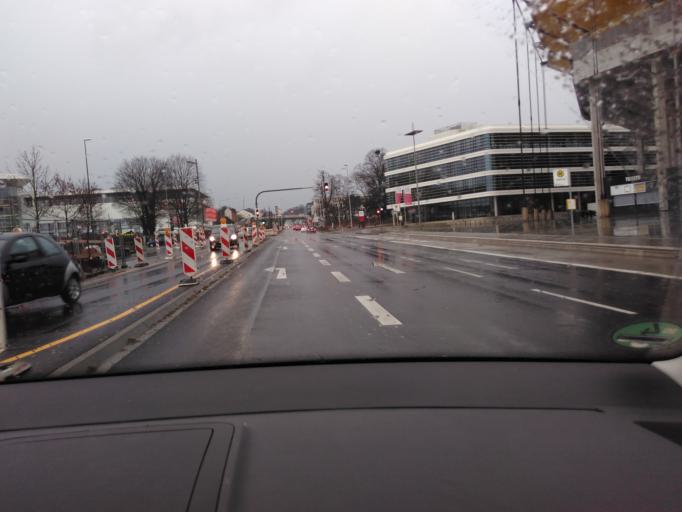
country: DE
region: North Rhine-Westphalia
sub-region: Regierungsbezirk Koln
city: Aachen
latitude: 50.7926
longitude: 6.0989
